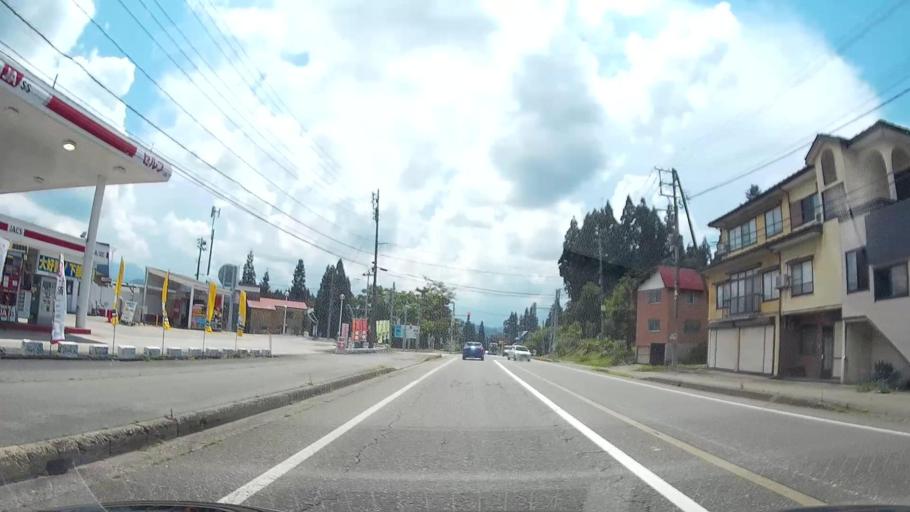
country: JP
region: Niigata
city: Tokamachi
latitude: 37.0303
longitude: 138.6669
